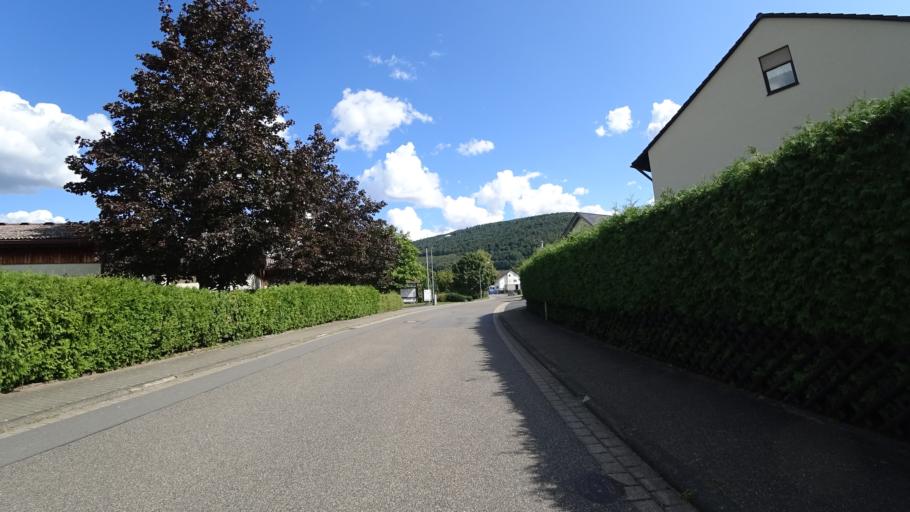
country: DE
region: Bavaria
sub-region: Regierungsbezirk Unterfranken
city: Burgstadt
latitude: 49.7086
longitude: 9.2753
